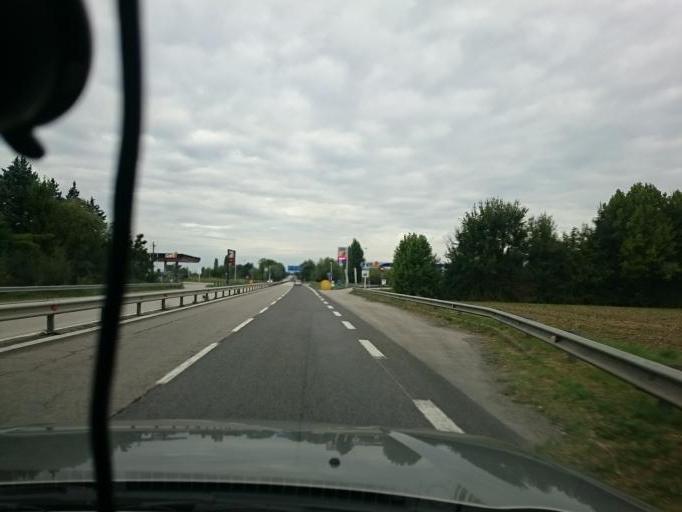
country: IT
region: Veneto
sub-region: Provincia di Padova
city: Mandriola-Sant'Agostino
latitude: 45.3774
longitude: 11.8416
